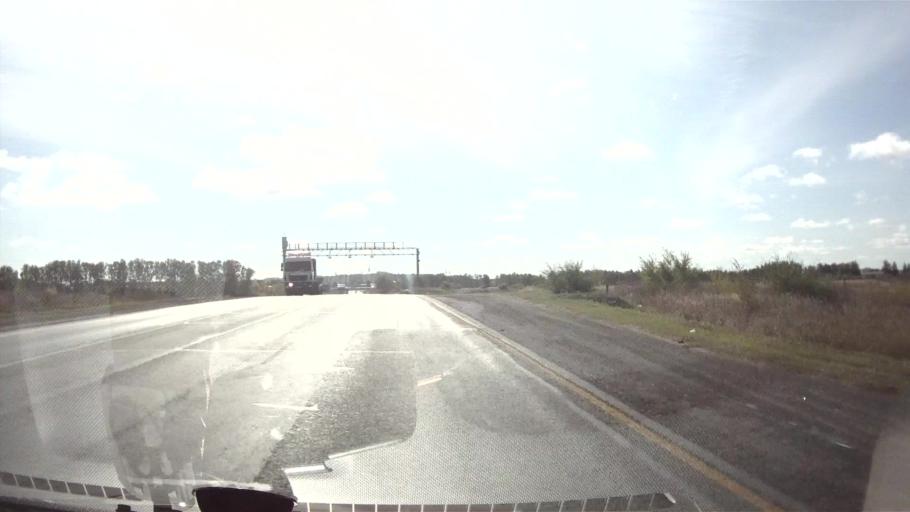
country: RU
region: Ulyanovsk
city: Isheyevka
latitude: 54.2989
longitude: 48.2465
